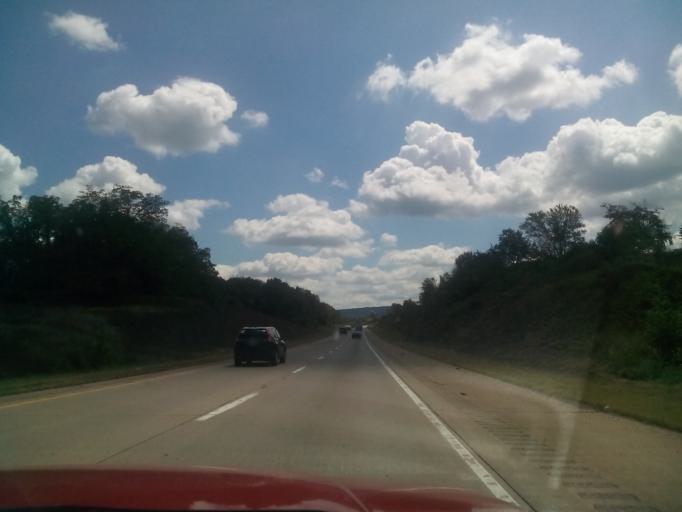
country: US
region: Pennsylvania
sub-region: Northumberland County
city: Milton
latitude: 40.9979
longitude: -76.7482
